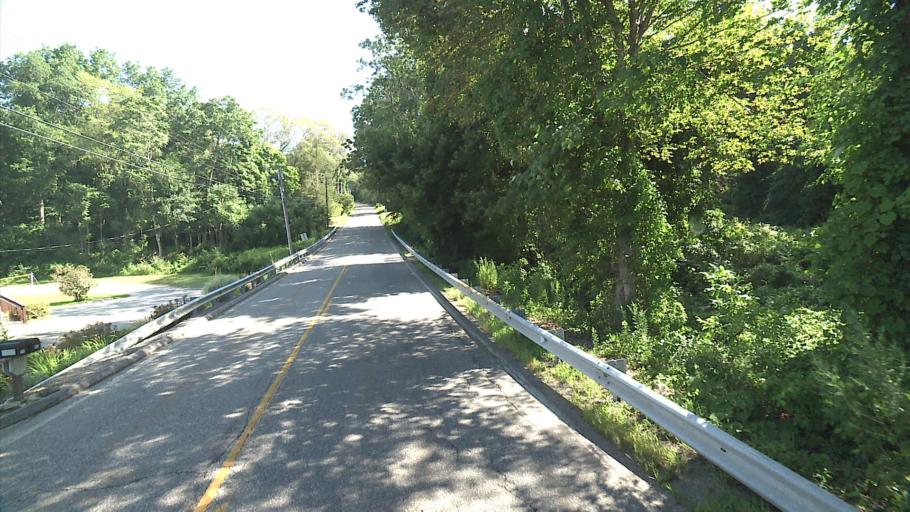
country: US
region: Connecticut
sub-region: New London County
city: Montville Center
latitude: 41.4758
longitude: -72.1628
